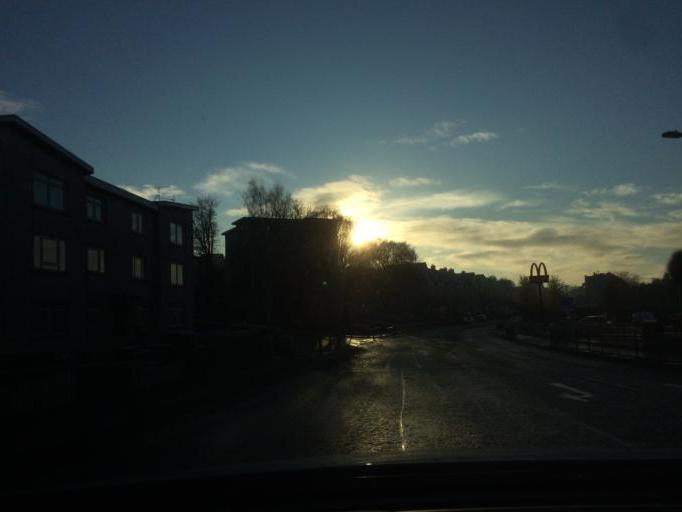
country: GB
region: Scotland
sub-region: East Renfrewshire
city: Giffnock
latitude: 55.8091
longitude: -4.3136
